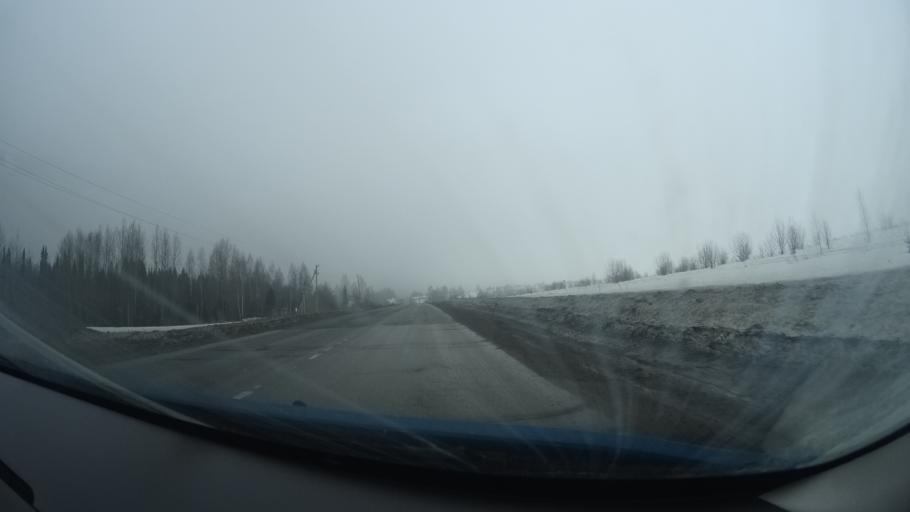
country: RU
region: Bashkortostan
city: Verkhniye Tatyshly
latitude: 56.4842
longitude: 55.7971
